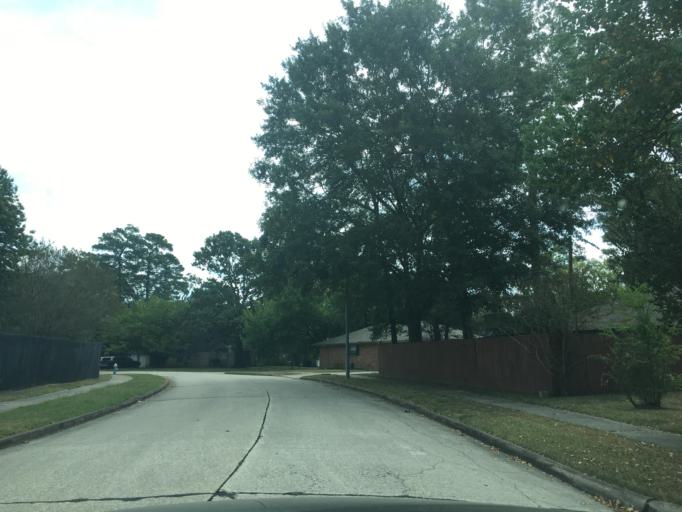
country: US
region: Texas
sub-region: Harris County
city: Spring
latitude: 30.1152
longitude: -95.4006
